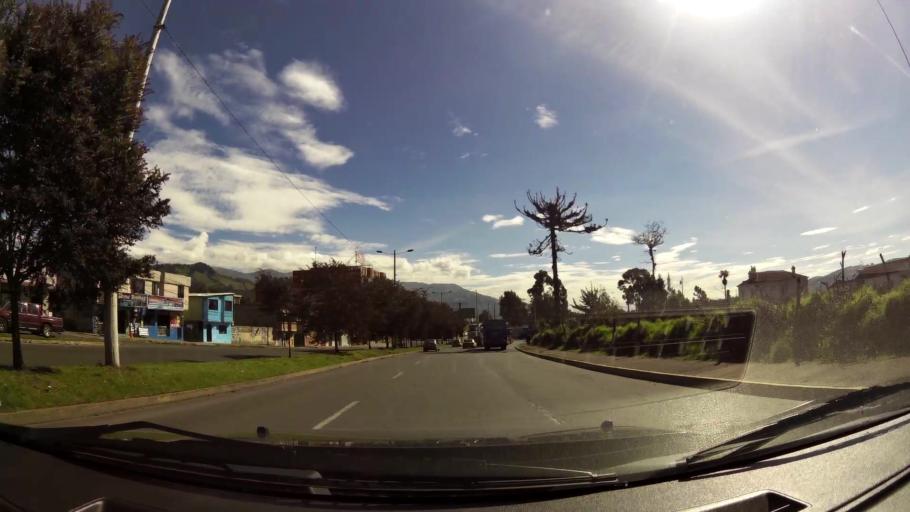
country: EC
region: Pichincha
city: Quito
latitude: -0.2929
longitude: -78.5587
